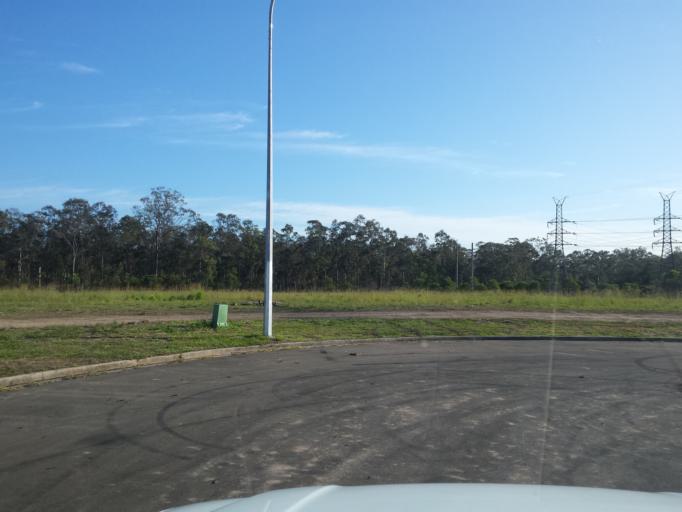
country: AU
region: Queensland
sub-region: Logan
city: Slacks Creek
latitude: -27.6595
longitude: 153.1298
